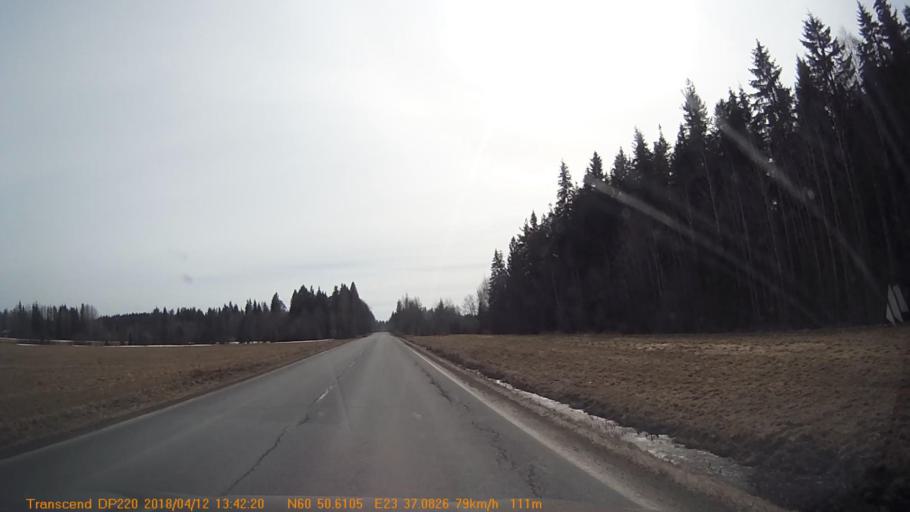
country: FI
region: Haeme
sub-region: Forssa
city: Forssa
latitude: 60.8427
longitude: 23.6181
